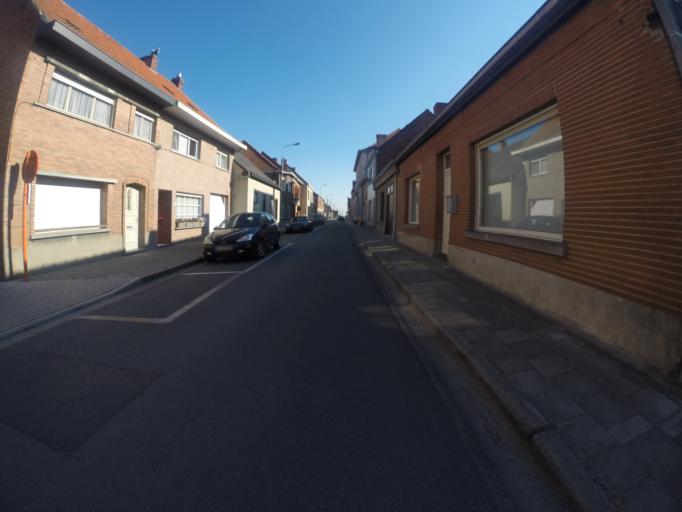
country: BE
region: Flanders
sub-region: Provincie West-Vlaanderen
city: Dentergem
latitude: 50.9953
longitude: 3.4220
